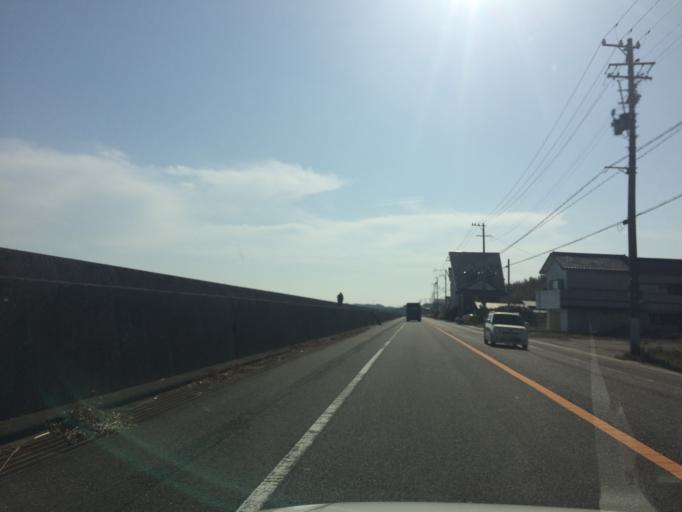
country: JP
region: Shizuoka
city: Sagara
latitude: 34.6541
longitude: 138.1936
